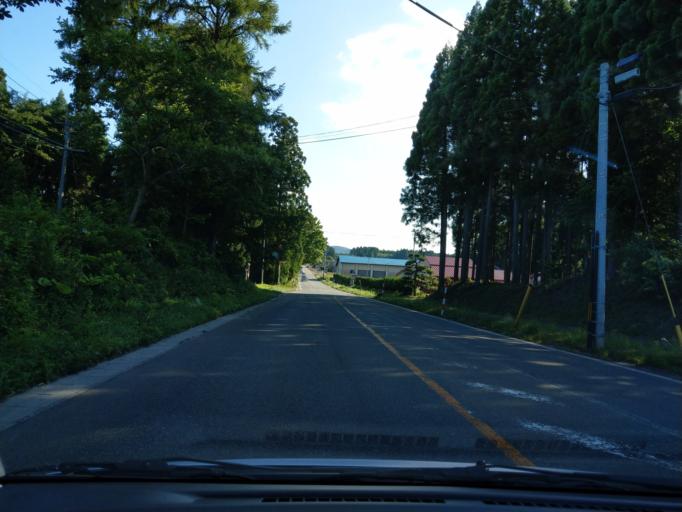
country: JP
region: Akita
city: Takanosu
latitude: 40.1469
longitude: 140.3915
